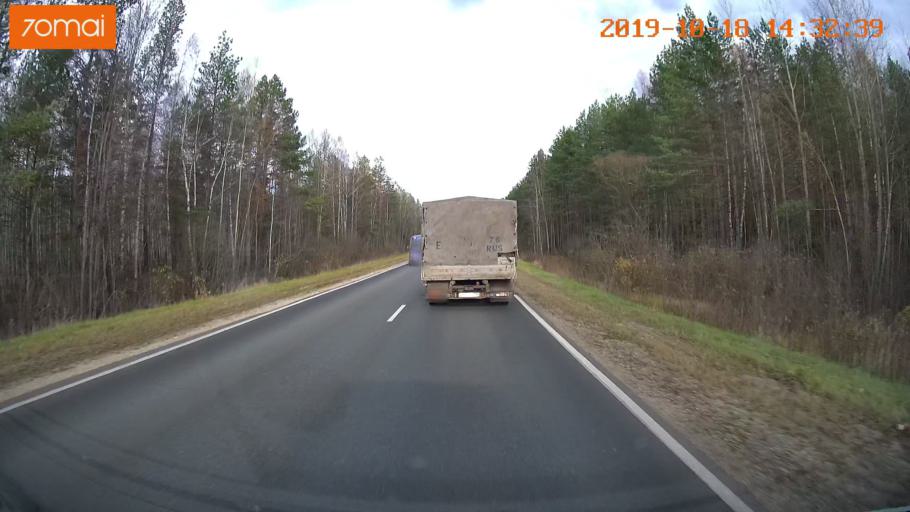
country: RU
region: Rjazan
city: Tuma
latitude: 55.1934
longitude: 40.5834
